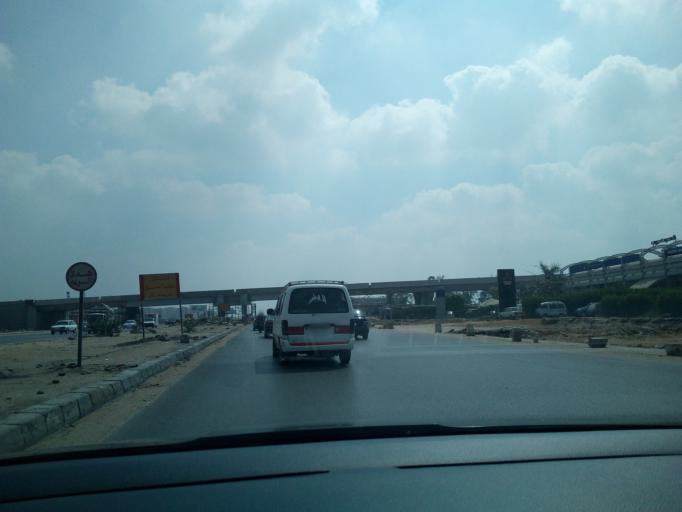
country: EG
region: Muhafazat al Qalyubiyah
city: Al Khankah
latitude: 30.1509
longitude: 31.4315
